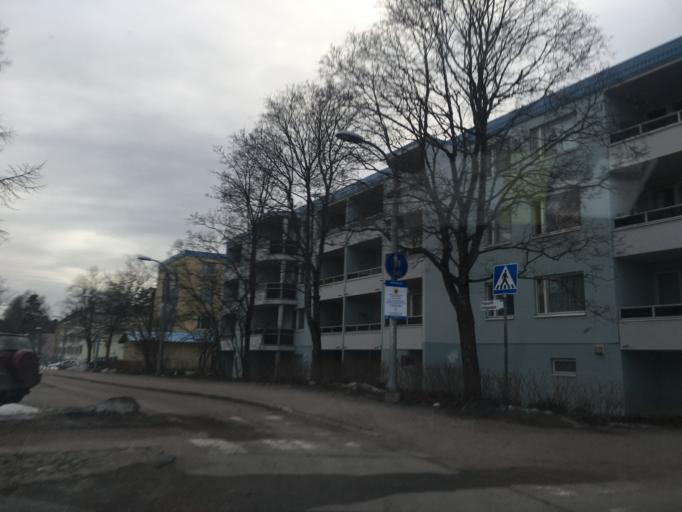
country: FI
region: Uusimaa
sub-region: Helsinki
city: Vantaa
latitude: 60.3236
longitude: 25.0760
